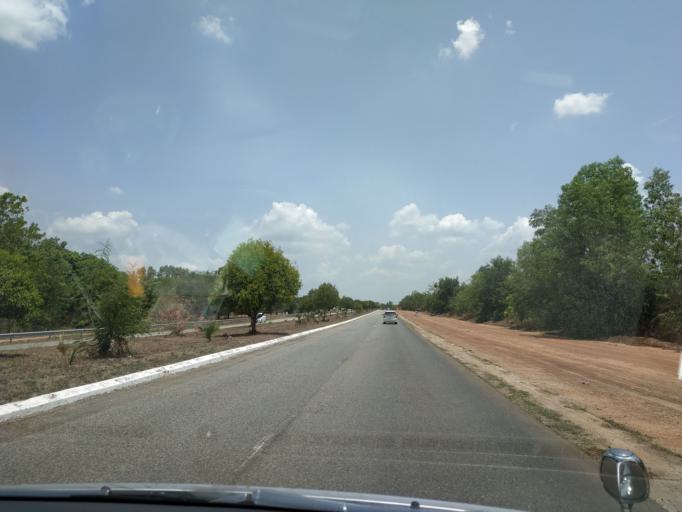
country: MM
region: Bago
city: Thanatpin
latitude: 17.1796
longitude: 96.1939
